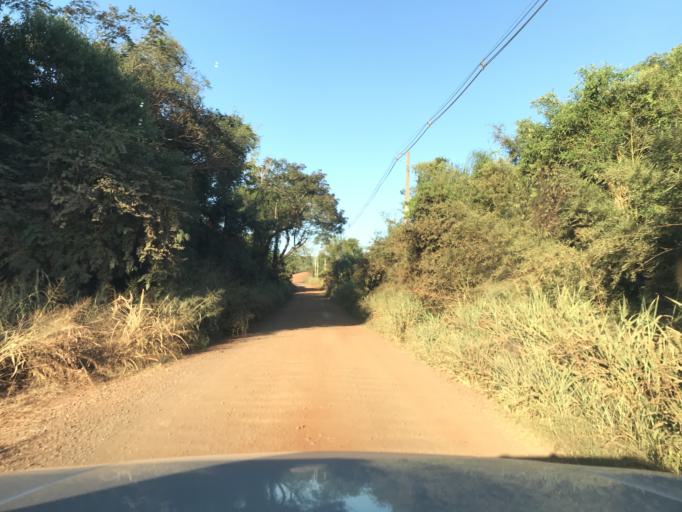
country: BR
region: Parana
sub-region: Palotina
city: Palotina
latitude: -24.2532
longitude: -53.7299
